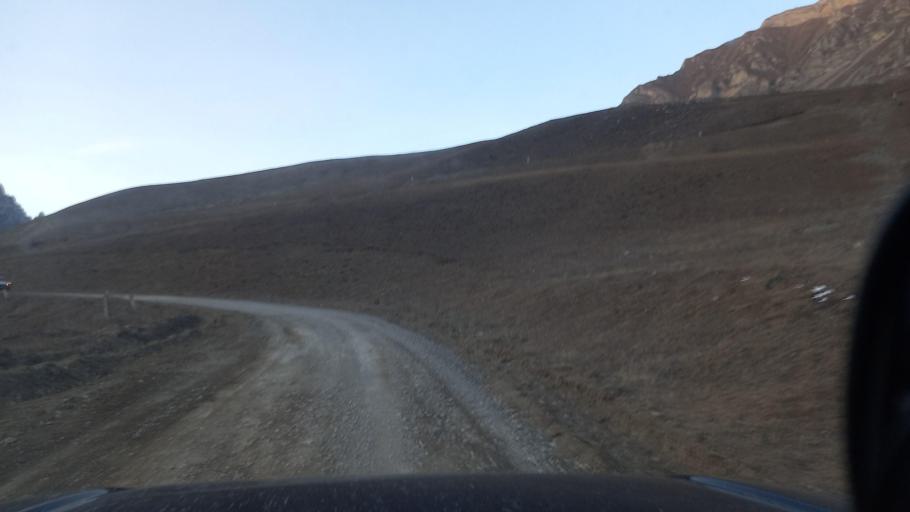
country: RU
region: Ingushetiya
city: Dzhayrakh
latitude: 42.8387
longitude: 44.5423
